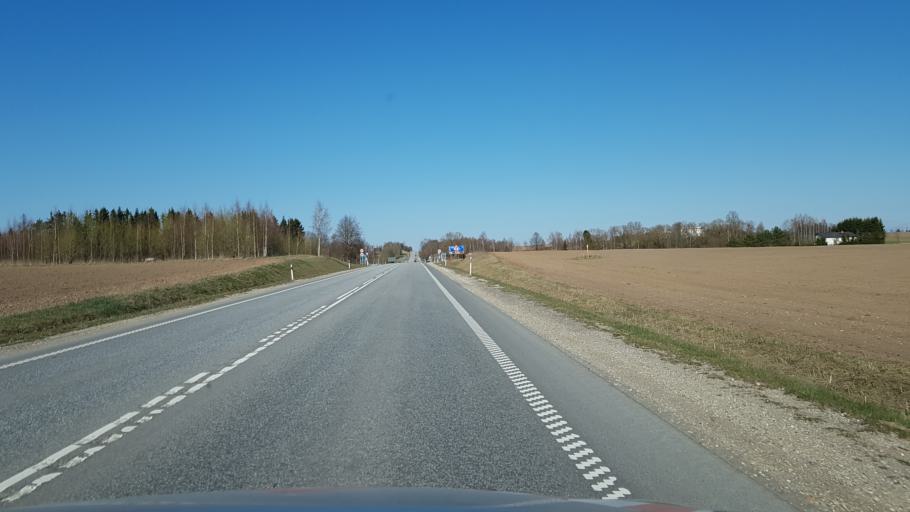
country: EE
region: Tartu
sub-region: Tartu linn
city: Tartu
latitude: 58.4235
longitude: 26.7787
